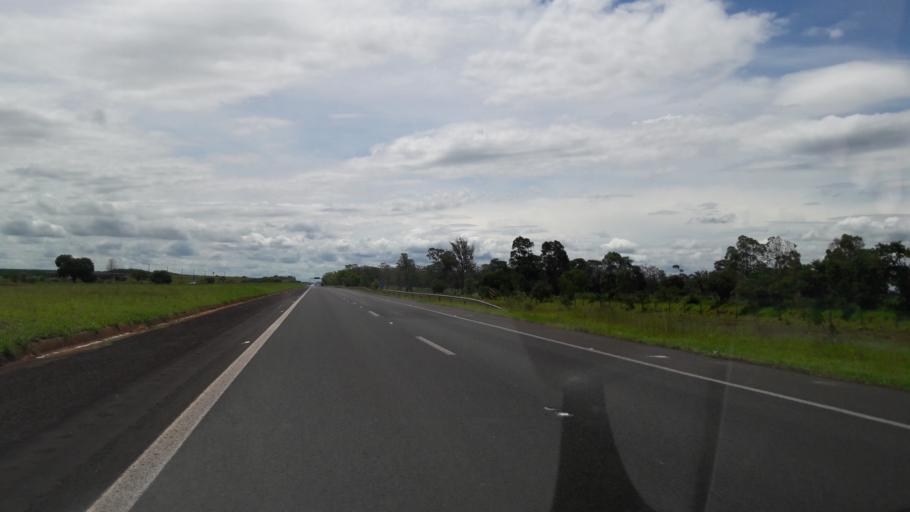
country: BR
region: Sao Paulo
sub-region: Avare
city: Avare
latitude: -22.9371
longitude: -48.9741
